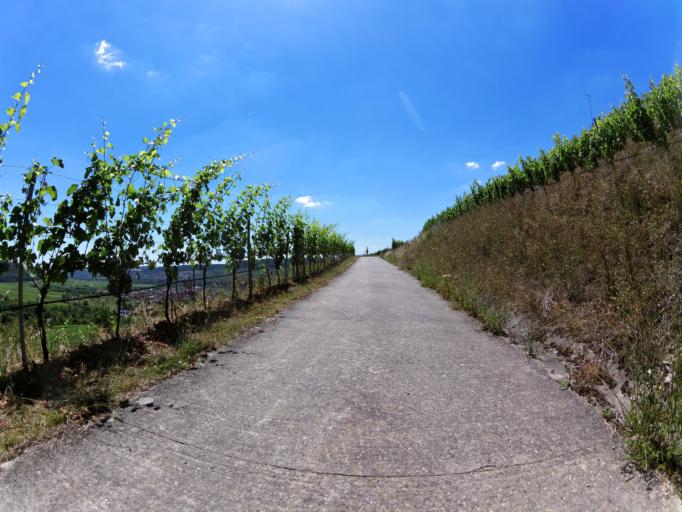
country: DE
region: Bavaria
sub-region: Regierungsbezirk Unterfranken
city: Thungersheim
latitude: 49.8900
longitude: 9.8502
